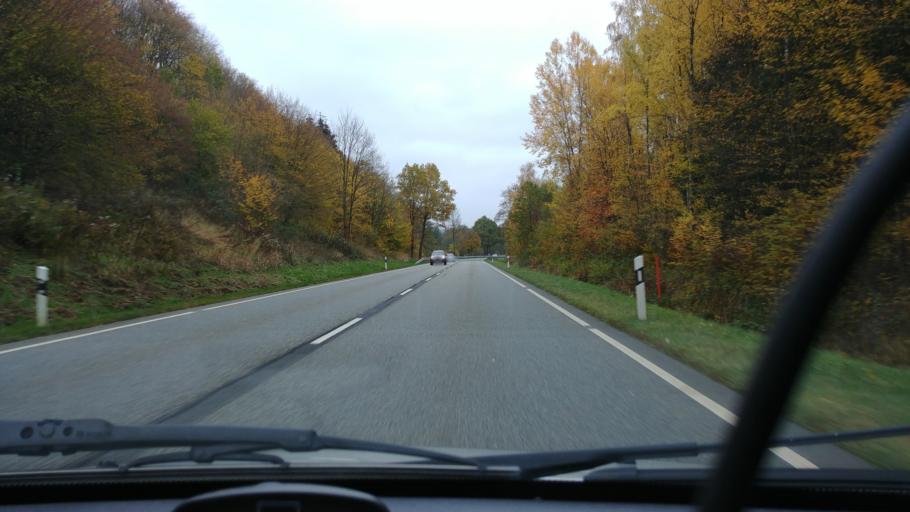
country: DE
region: Rheinland-Pfalz
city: Norken
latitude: 50.6624
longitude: 7.8803
